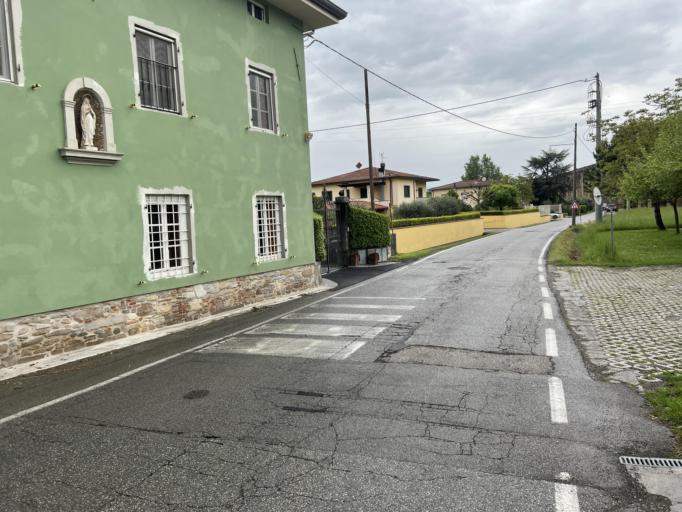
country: IT
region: Tuscany
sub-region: Provincia di Lucca
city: Lucca
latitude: 43.8158
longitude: 10.5167
